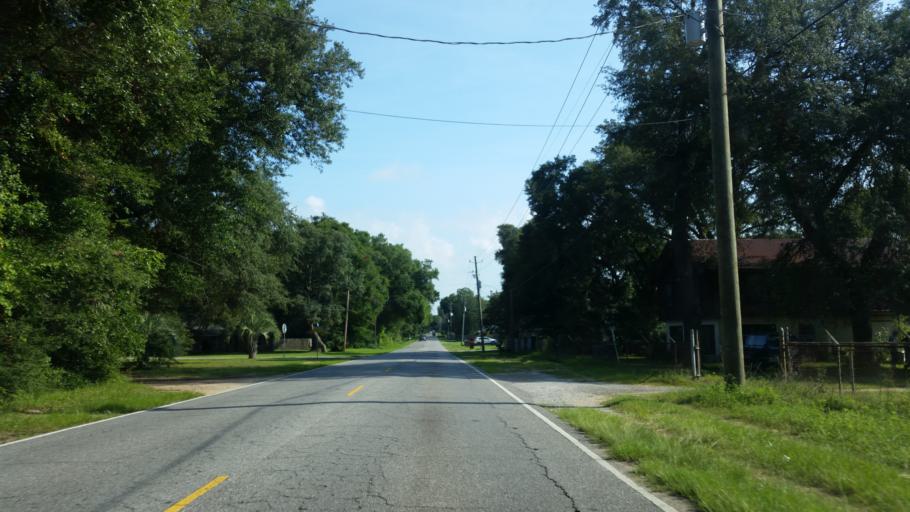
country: US
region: Florida
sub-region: Escambia County
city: Bellview
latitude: 30.4551
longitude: -87.3160
